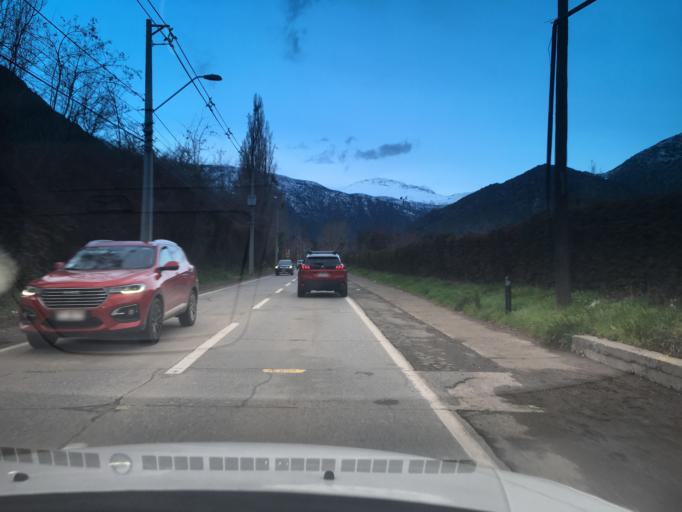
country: CL
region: Santiago Metropolitan
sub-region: Provincia de Cordillera
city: Puente Alto
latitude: -33.5882
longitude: -70.3879
